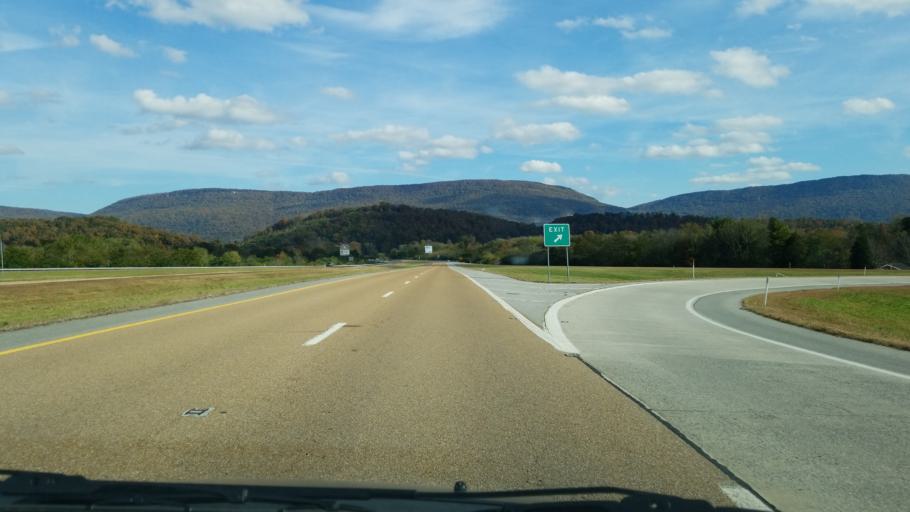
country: US
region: Tennessee
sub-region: Sequatchie County
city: Dunlap
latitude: 35.3950
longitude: -85.3732
